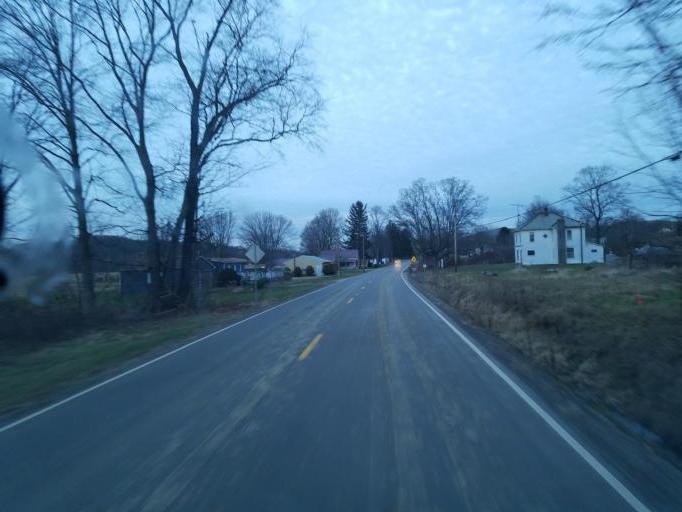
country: US
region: Ohio
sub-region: Muskingum County
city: Dresden
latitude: 40.1977
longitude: -82.0466
